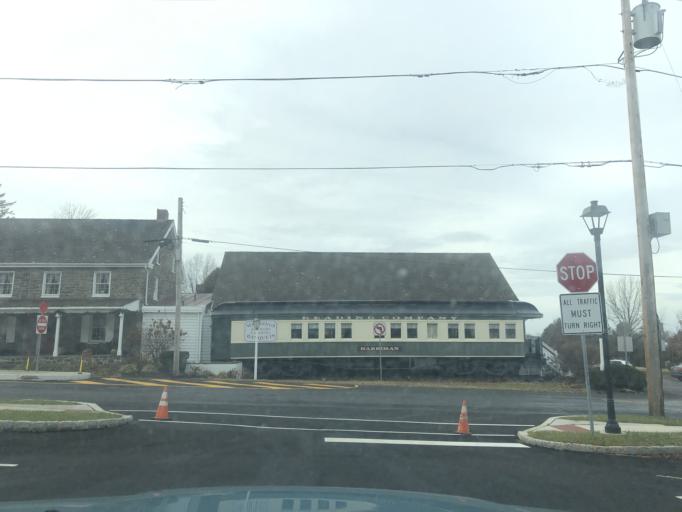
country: US
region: Pennsylvania
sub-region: Montgomery County
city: Harleysville
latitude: 40.2622
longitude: -75.4065
